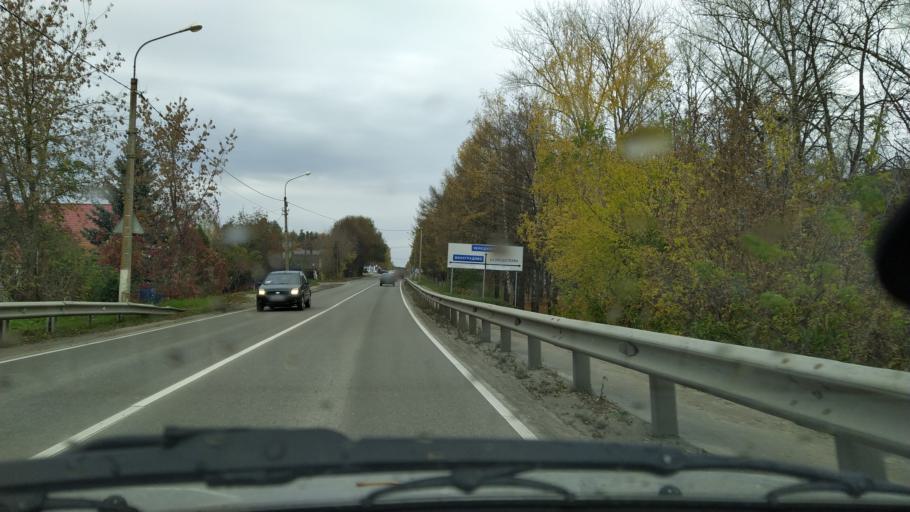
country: RU
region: Moskovskaya
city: Voskresensk
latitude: 55.3240
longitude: 38.6541
